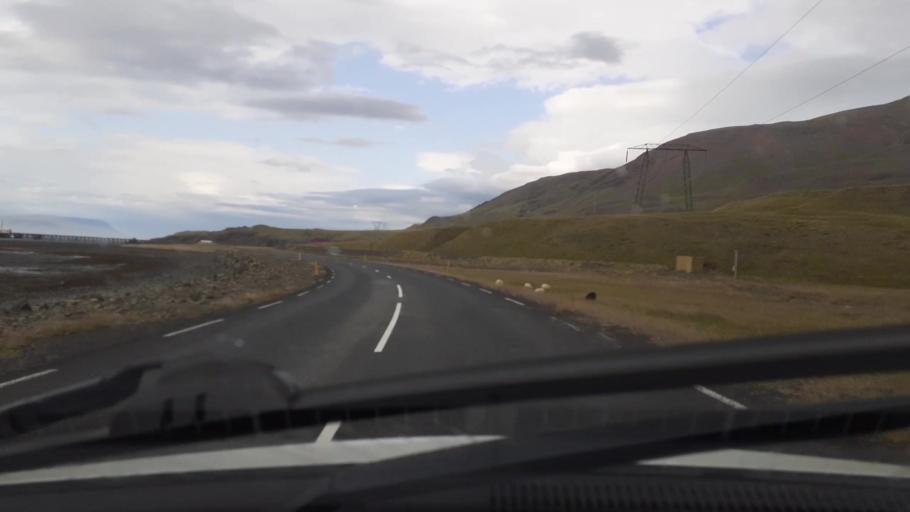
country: IS
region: Capital Region
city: Mosfellsbaer
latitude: 64.3975
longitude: -21.4442
